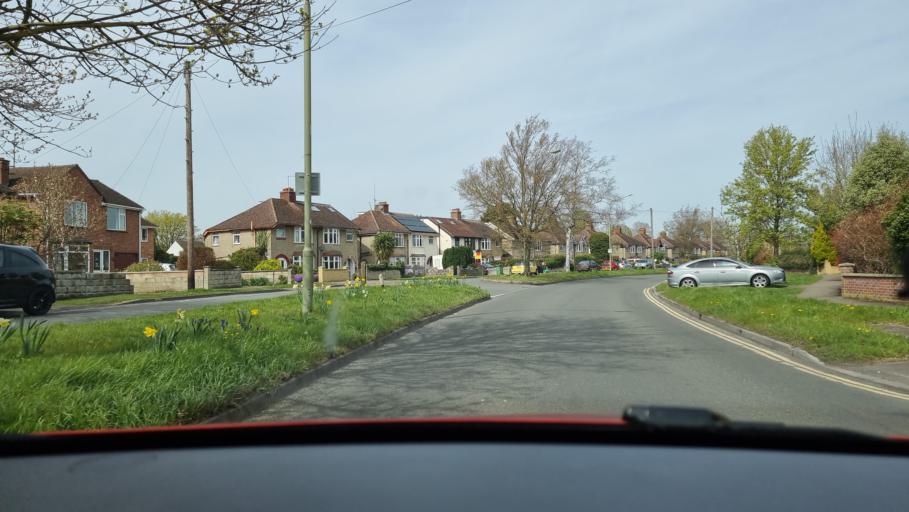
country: GB
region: England
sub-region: Oxfordshire
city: Oxford
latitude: 51.7687
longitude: -1.2373
